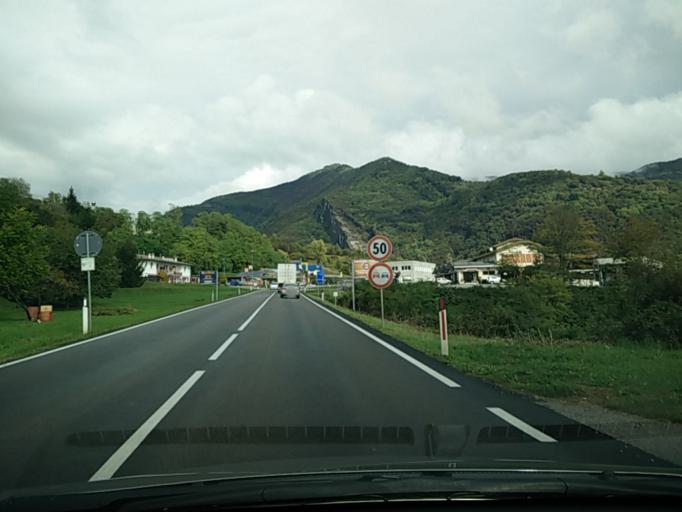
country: IT
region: Veneto
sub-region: Provincia di Belluno
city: Quero
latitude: 45.9165
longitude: 11.9418
